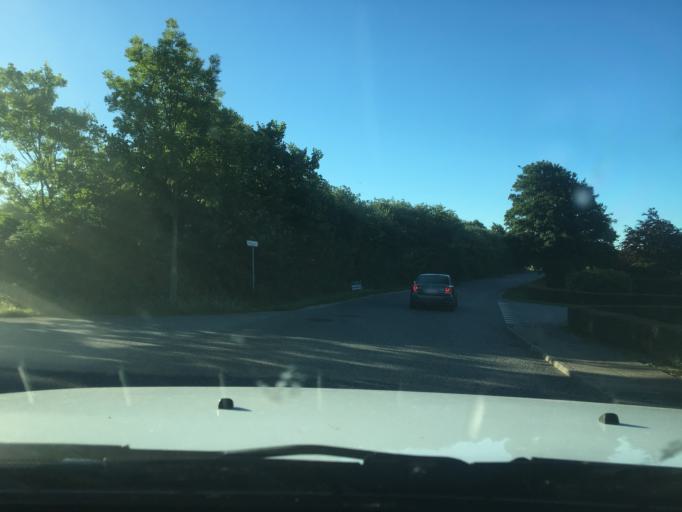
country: DK
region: Central Jutland
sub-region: Randers Kommune
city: Langa
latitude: 56.3939
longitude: 9.9585
